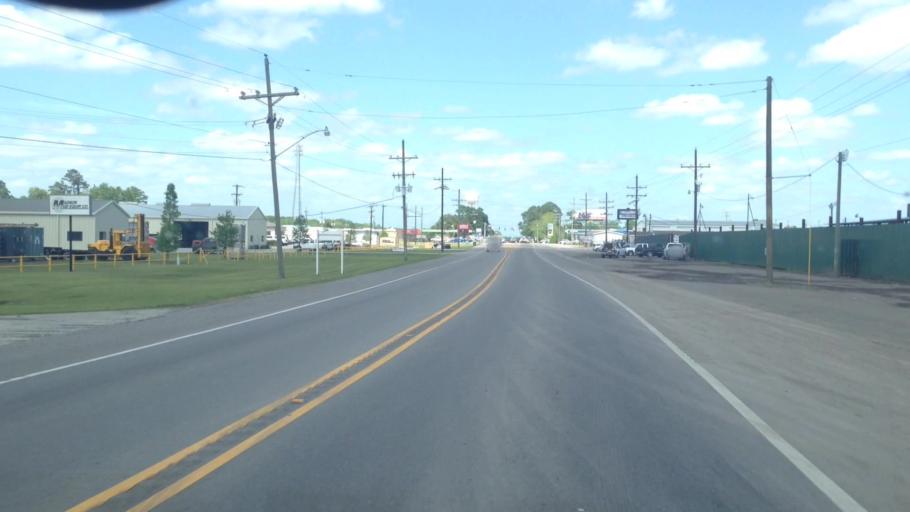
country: US
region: Louisiana
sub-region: Terrebonne Parish
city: Houma
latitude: 29.6423
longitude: -90.6902
